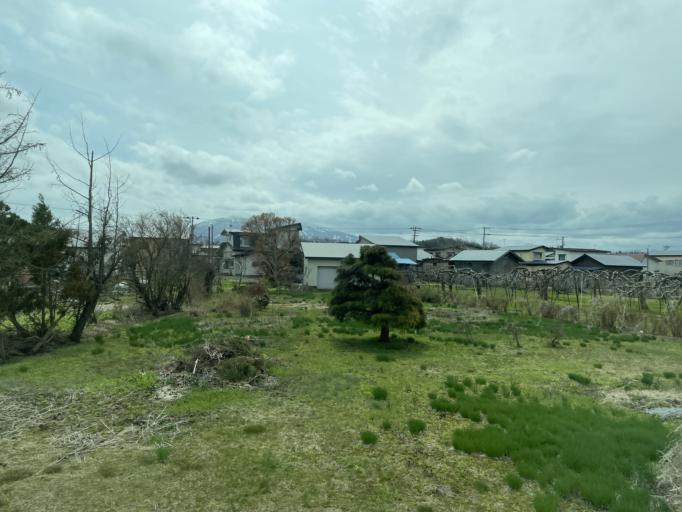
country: JP
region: Aomori
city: Shimokizukuri
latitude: 40.7835
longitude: 140.3228
